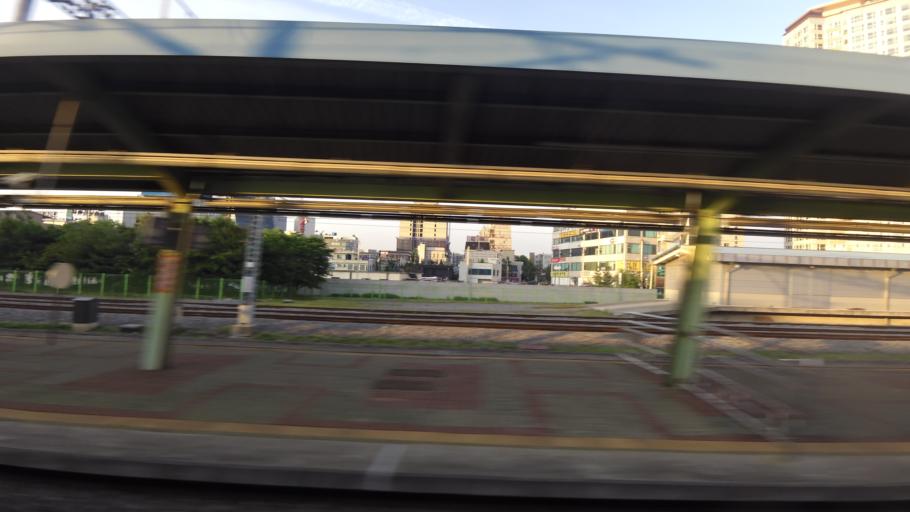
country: KR
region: Chungcheongnam-do
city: Seonghwan
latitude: 36.9892
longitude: 127.0870
